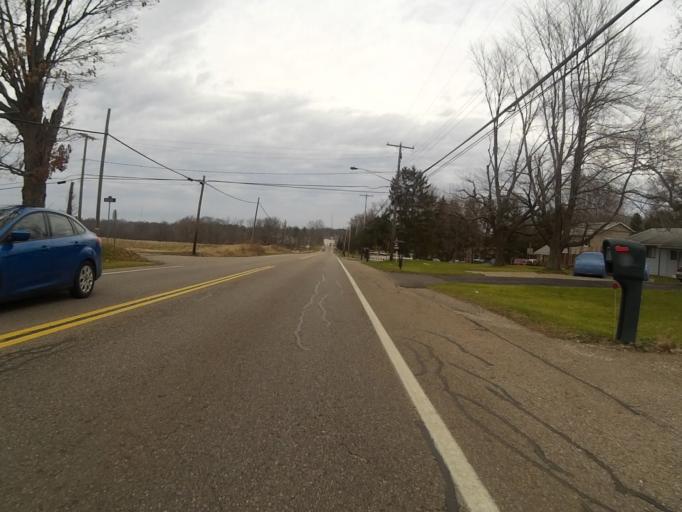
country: US
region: Ohio
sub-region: Portage County
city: Brimfield
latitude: 41.0908
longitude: -81.3465
